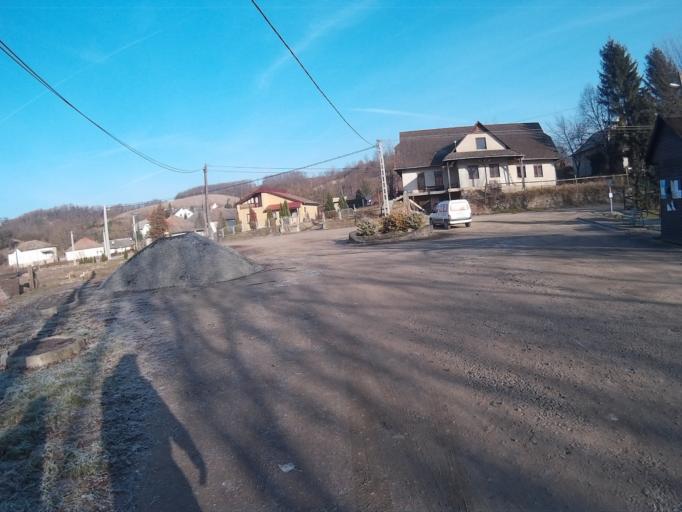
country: HU
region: Nograd
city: Bercel
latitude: 47.9273
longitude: 19.4109
